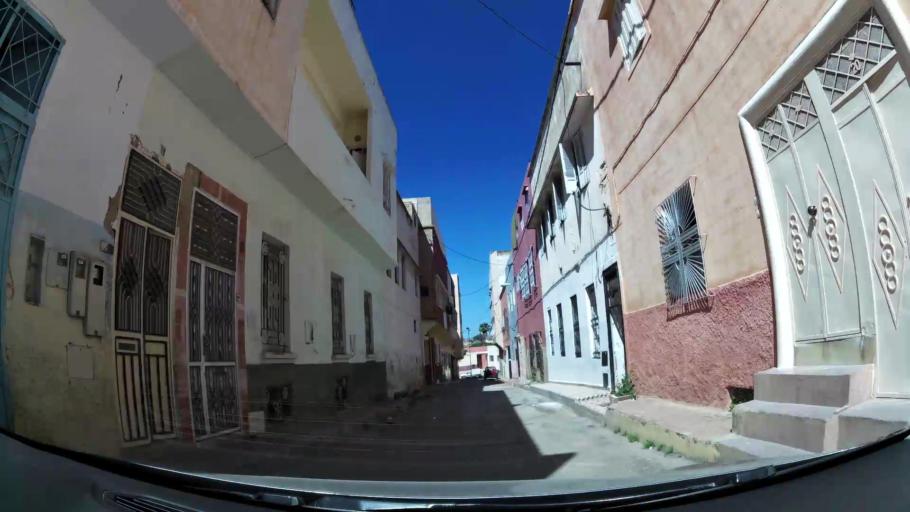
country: MA
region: Meknes-Tafilalet
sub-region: Meknes
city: Meknes
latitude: 33.8881
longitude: -5.5692
